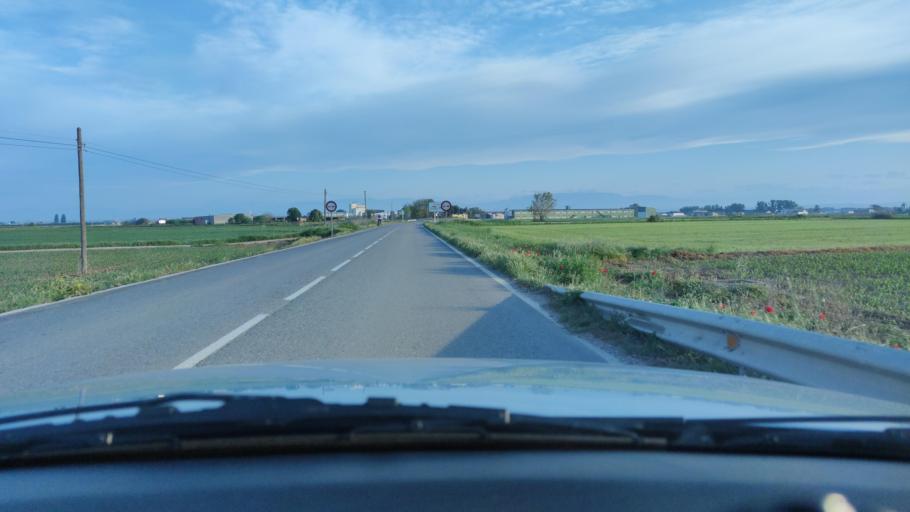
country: ES
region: Catalonia
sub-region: Provincia de Lleida
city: Ivars d'Urgell
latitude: 41.6699
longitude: 0.9903
